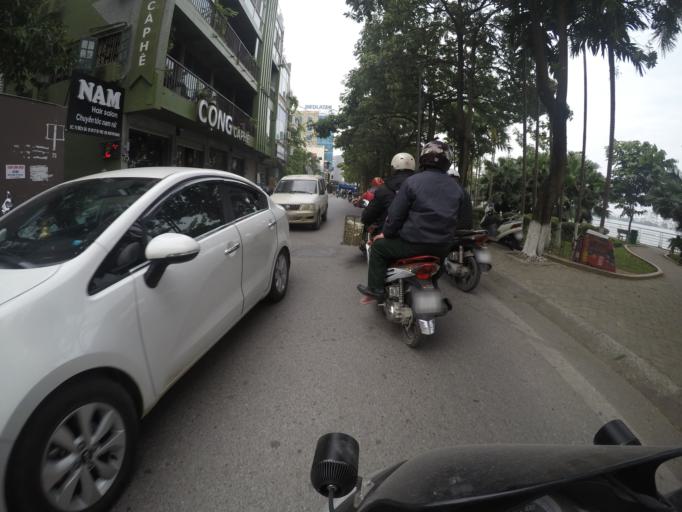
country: VN
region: Ha Noi
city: Cau Giay
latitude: 21.0465
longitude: 105.8147
